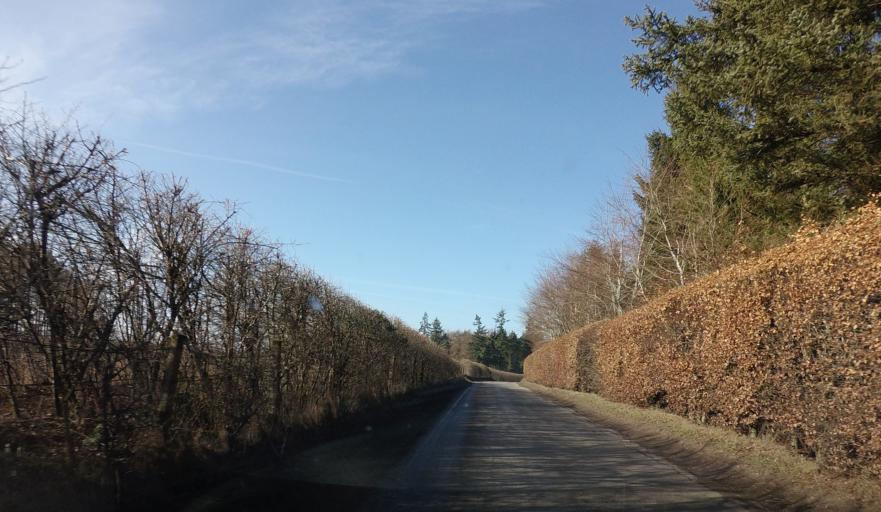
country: GB
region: Scotland
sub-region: Perth and Kinross
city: Stanley
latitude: 56.5265
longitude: -3.4147
